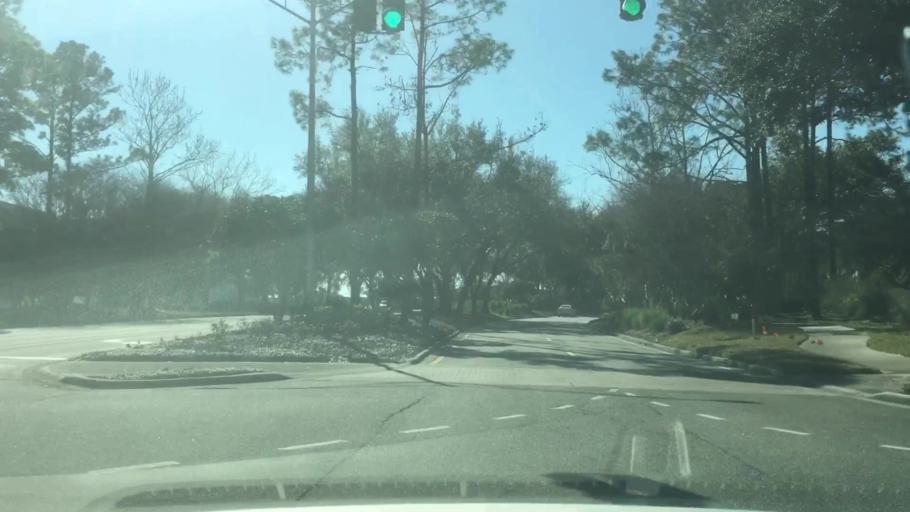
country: US
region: Florida
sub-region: Duval County
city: Jacksonville
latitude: 30.2413
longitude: -81.5470
